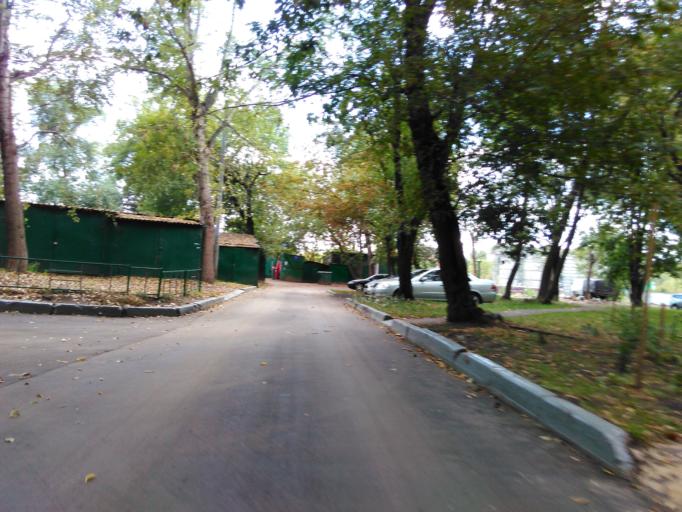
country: RU
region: Moscow
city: Novyye Cheremushki
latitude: 55.6901
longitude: 37.6116
